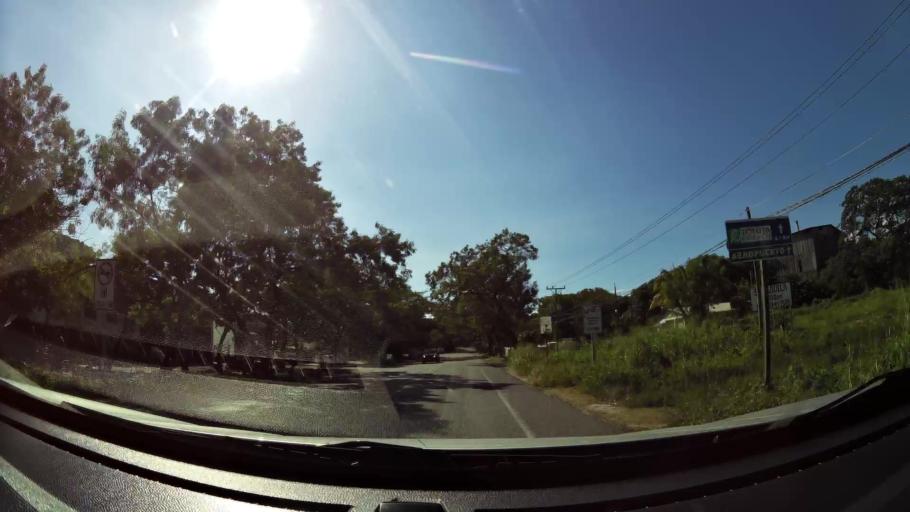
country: CR
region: Guanacaste
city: Liberia
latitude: 10.6249
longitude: -85.4495
